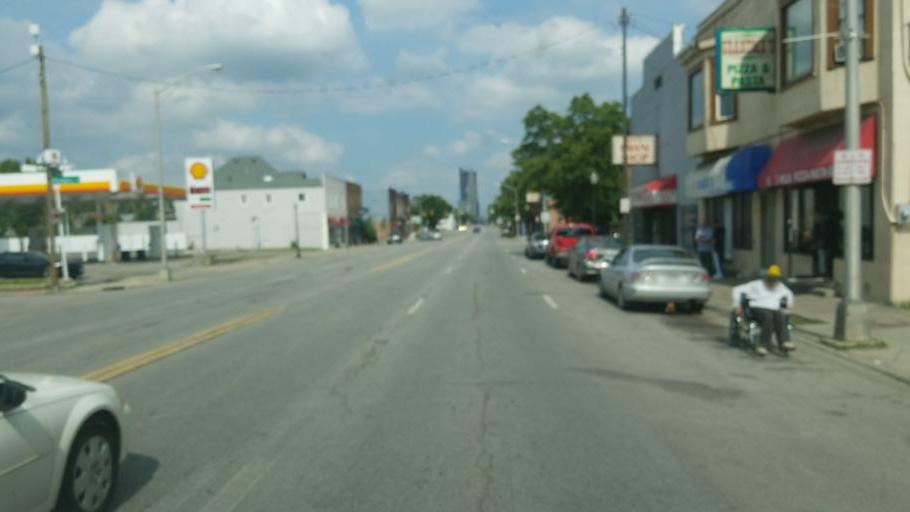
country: US
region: Ohio
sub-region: Franklin County
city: Grandview Heights
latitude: 39.9588
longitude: -83.0278
